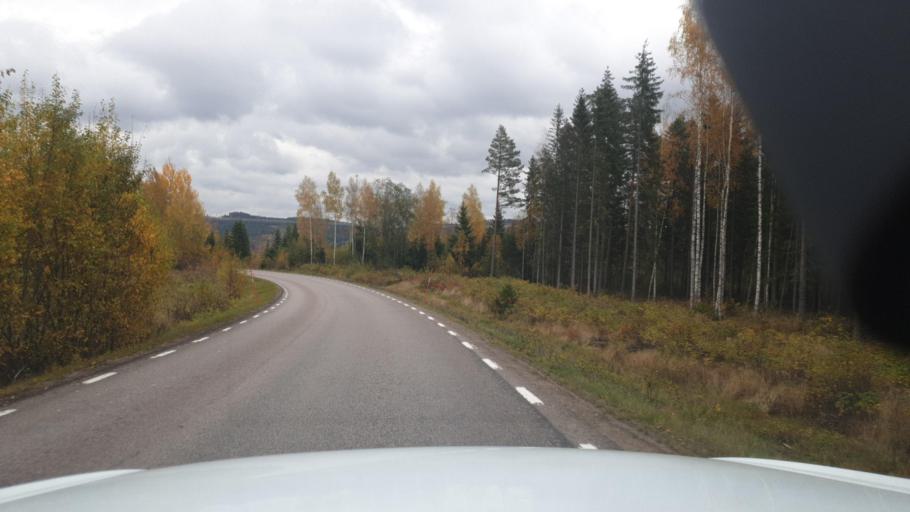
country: SE
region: Vaermland
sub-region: Torsby Kommun
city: Torsby
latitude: 59.9202
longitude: 12.8853
